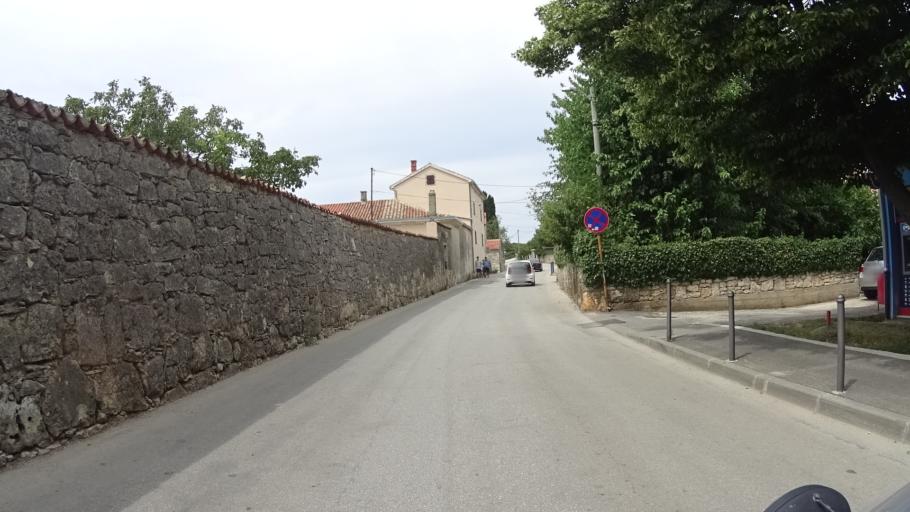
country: HR
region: Istarska
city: Medulin
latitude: 44.8027
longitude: 13.9100
